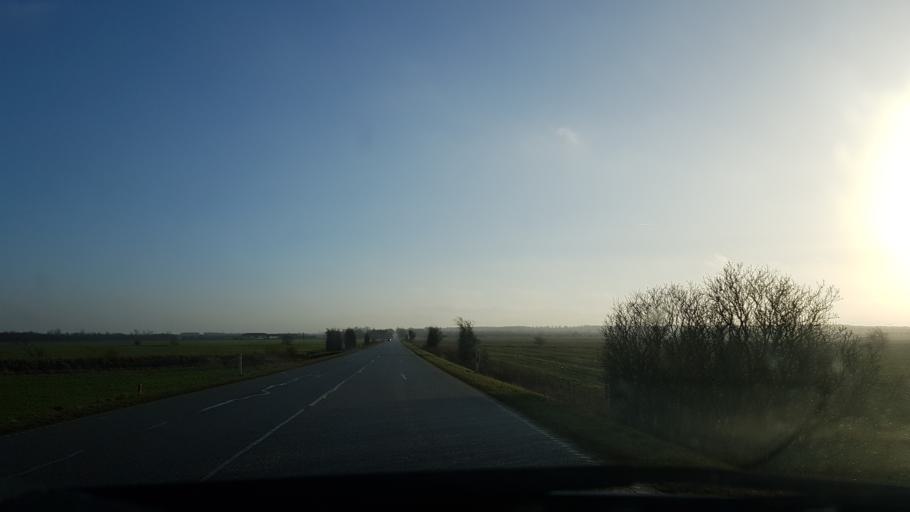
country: DK
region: South Denmark
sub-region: Tonder Kommune
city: Toftlund
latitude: 55.2465
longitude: 9.1532
